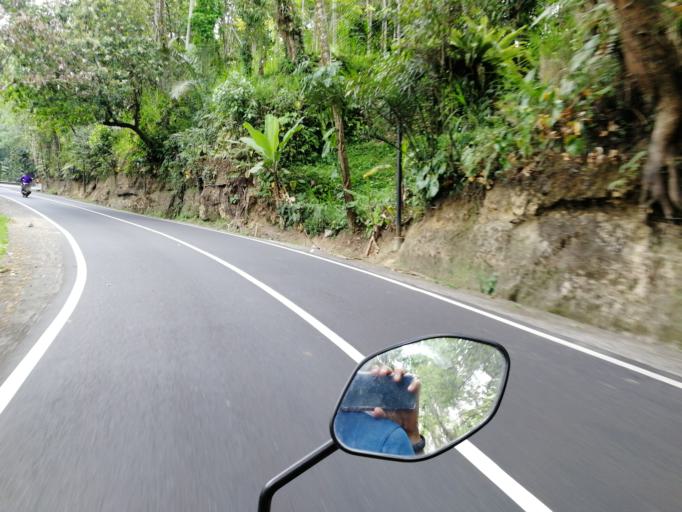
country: ID
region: Bali
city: Banjar Geriana Kangin
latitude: -8.4266
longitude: 115.4362
